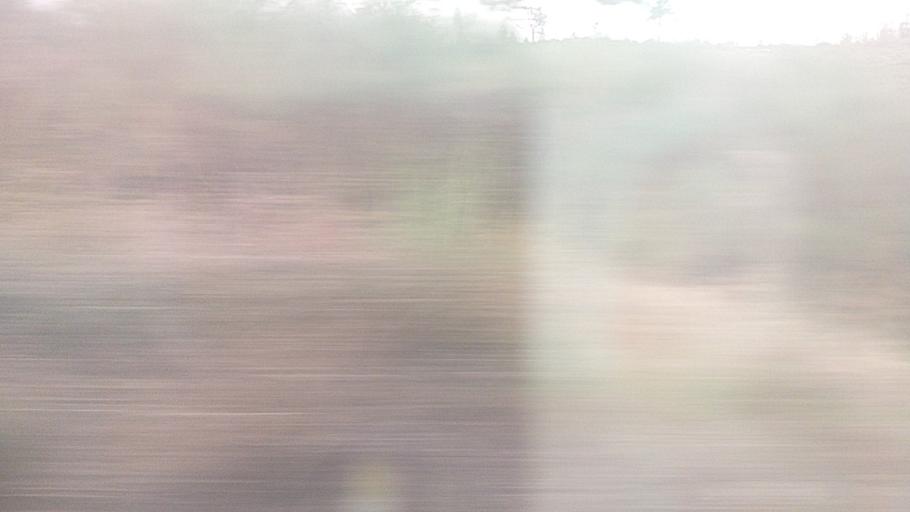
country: PT
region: Guarda
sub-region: Fornos de Algodres
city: Fornos de Algodres
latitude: 40.6002
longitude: -7.5521
